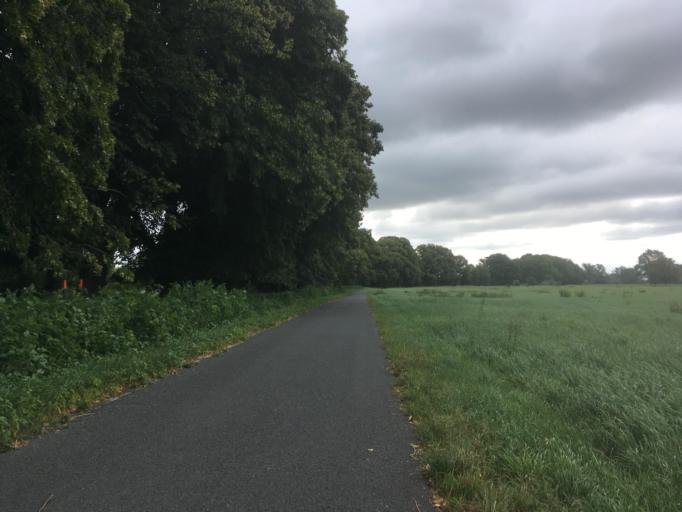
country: DE
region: Saxony
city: Zeithain
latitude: 51.3082
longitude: 13.3421
